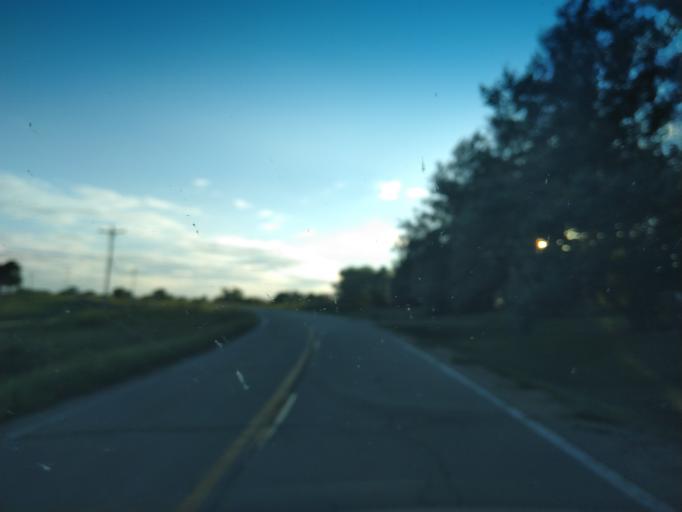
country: US
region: Iowa
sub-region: Jackson County
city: Maquoketa
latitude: 42.1634
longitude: -90.7402
